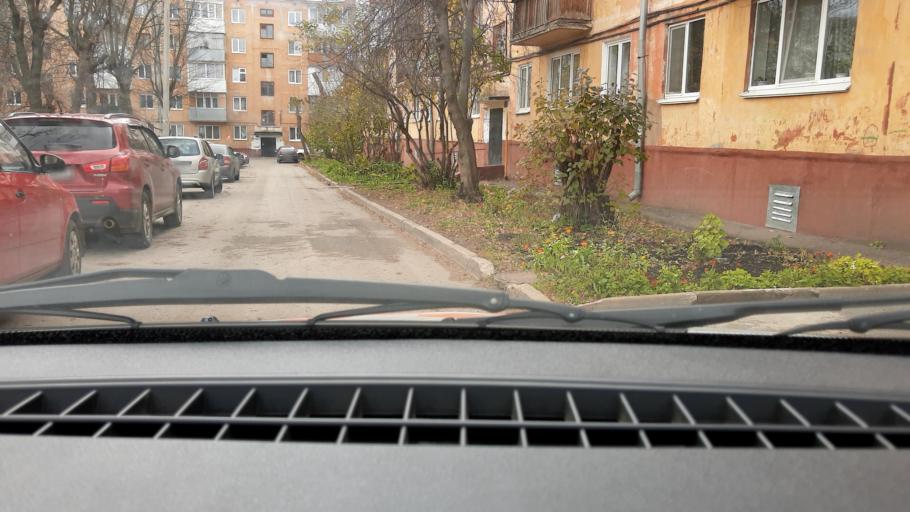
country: RU
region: Bashkortostan
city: Ufa
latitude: 54.8099
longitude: 56.0949
